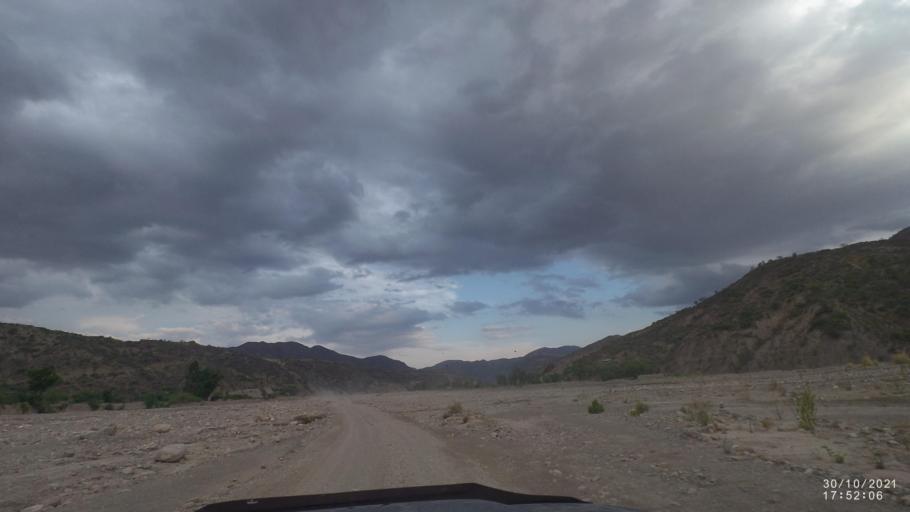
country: BO
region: Cochabamba
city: Sipe Sipe
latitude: -17.5374
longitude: -66.5013
